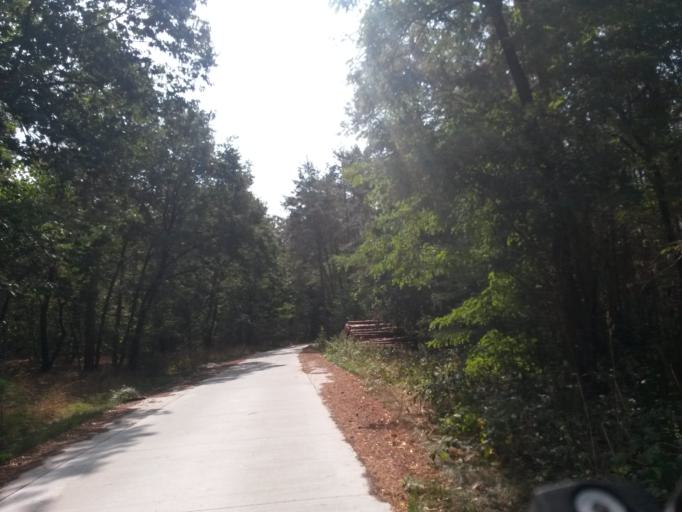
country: DE
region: Saxony-Anhalt
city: Muhlanger
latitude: 51.8155
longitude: 12.7732
